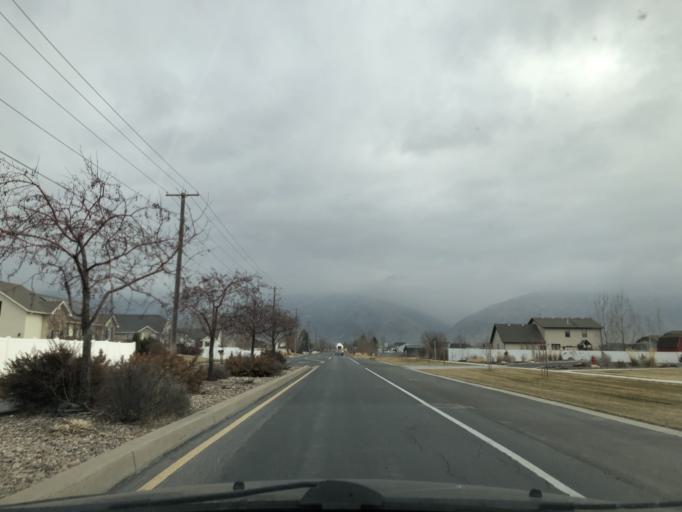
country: US
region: Utah
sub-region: Cache County
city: Nibley
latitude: 41.6752
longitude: -111.8703
